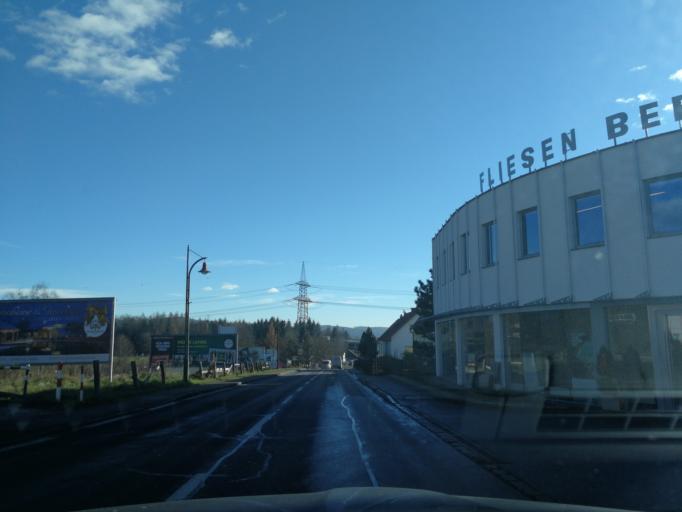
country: AT
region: Styria
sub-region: Politischer Bezirk Weiz
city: Gleisdorf
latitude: 47.0949
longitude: 15.7267
